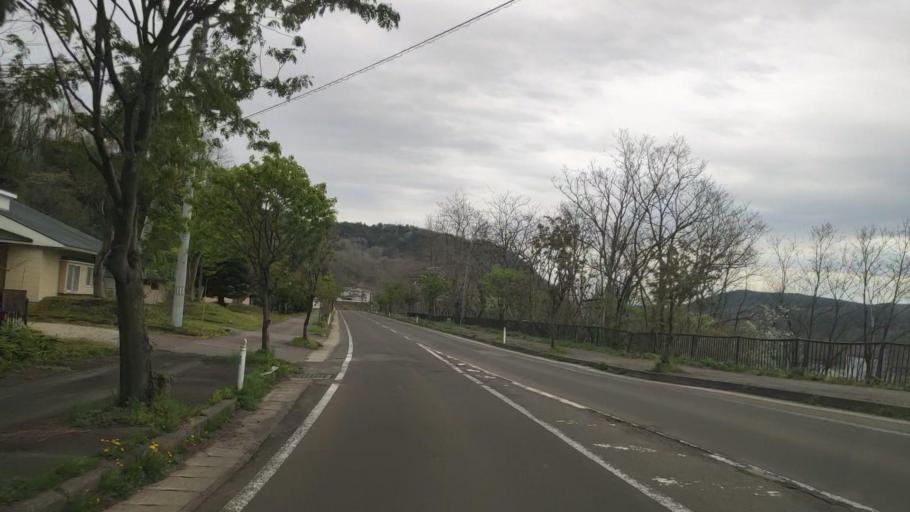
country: JP
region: Akita
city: Hanawa
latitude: 40.3291
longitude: 140.7471
